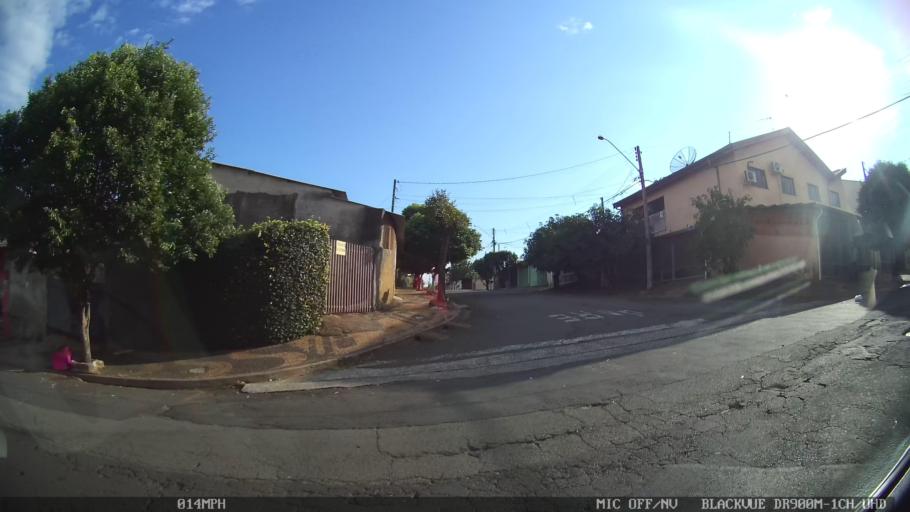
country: BR
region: Sao Paulo
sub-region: Americana
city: Americana
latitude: -22.7277
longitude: -47.3683
